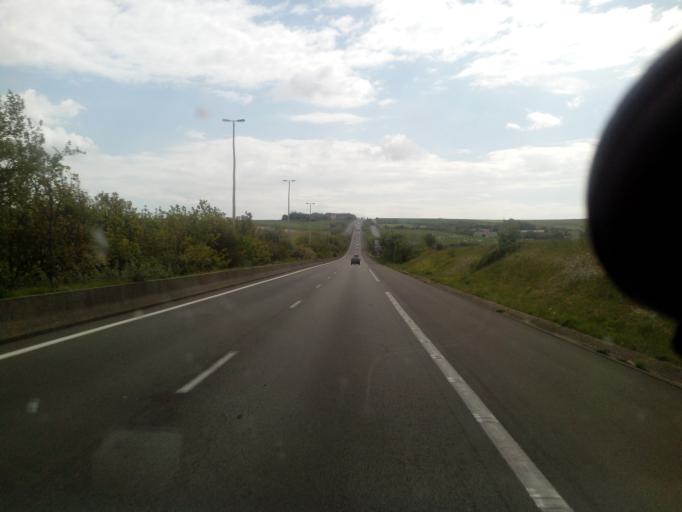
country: FR
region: Nord-Pas-de-Calais
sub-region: Departement du Pas-de-Calais
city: Sangatte
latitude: 50.8953
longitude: 1.7629
